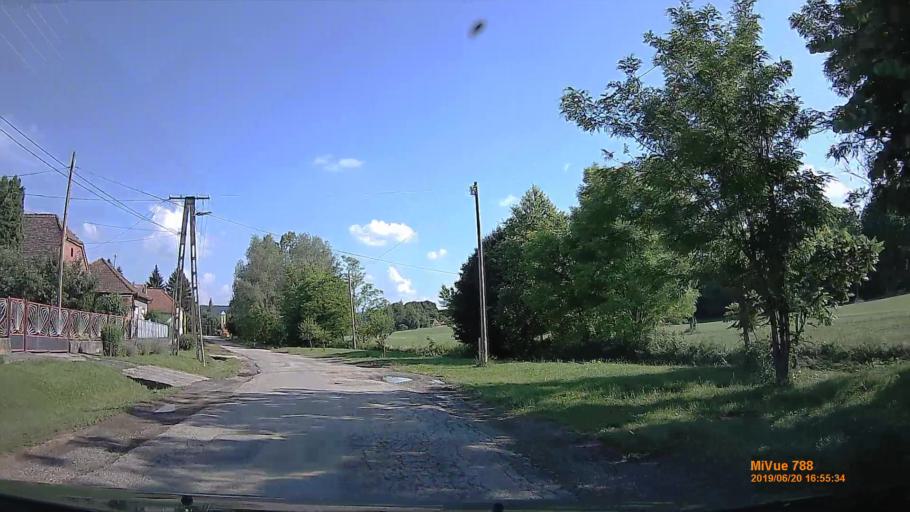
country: HU
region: Baranya
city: Buekkoesd
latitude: 46.1546
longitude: 18.0577
